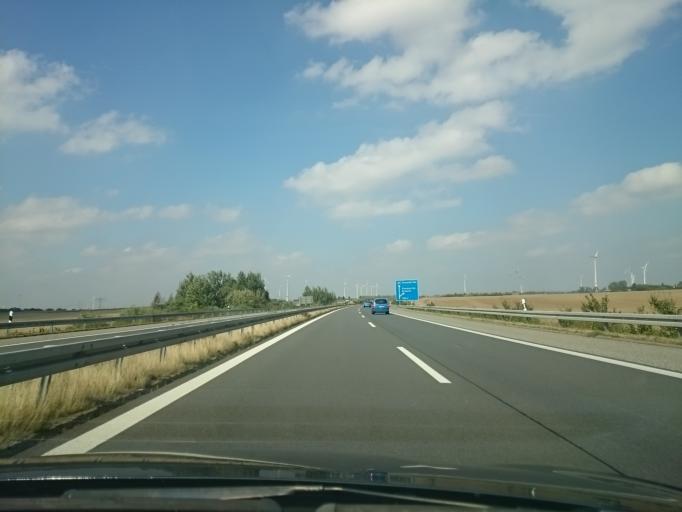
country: DE
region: Brandenburg
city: Schenkenberg
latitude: 53.3478
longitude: 13.9754
